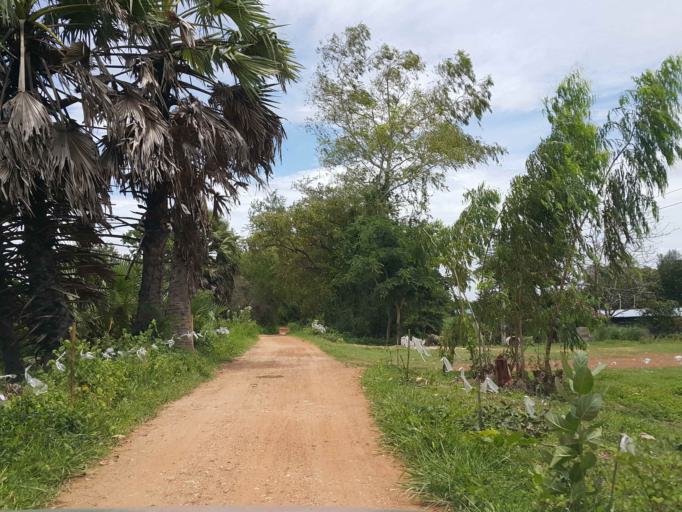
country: TH
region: Sukhothai
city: Ban Na
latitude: 17.0040
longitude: 99.6979
